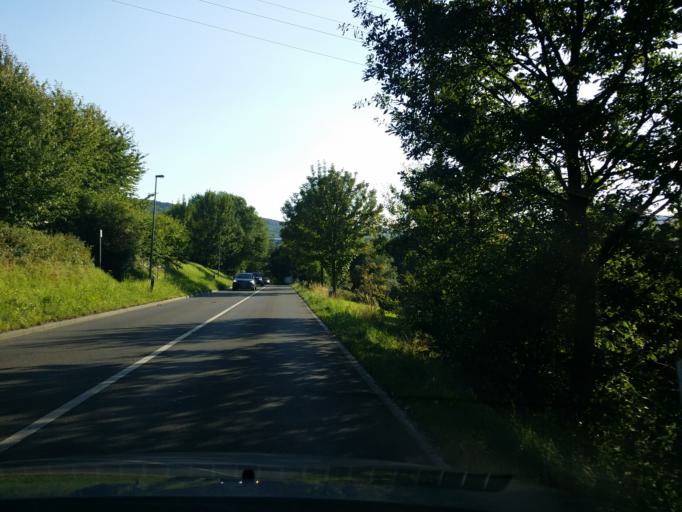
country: DE
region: Hesse
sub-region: Regierungsbezirk Darmstadt
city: Niedernhausen
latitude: 50.1657
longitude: 8.3242
